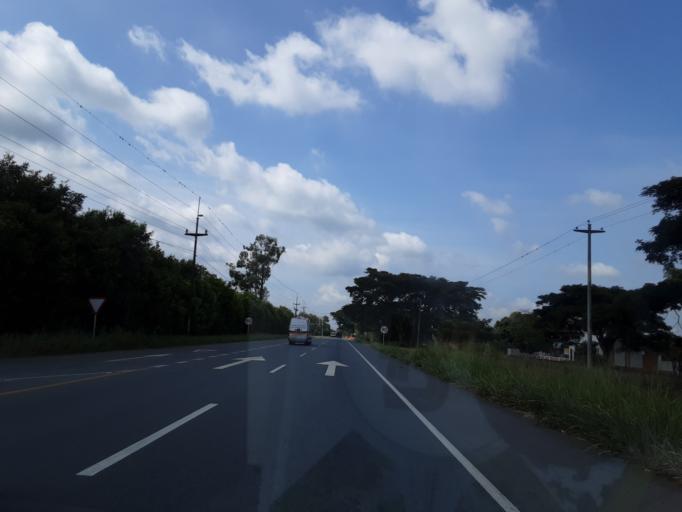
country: CO
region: Valle del Cauca
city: Guacari
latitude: 3.7382
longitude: -76.3240
